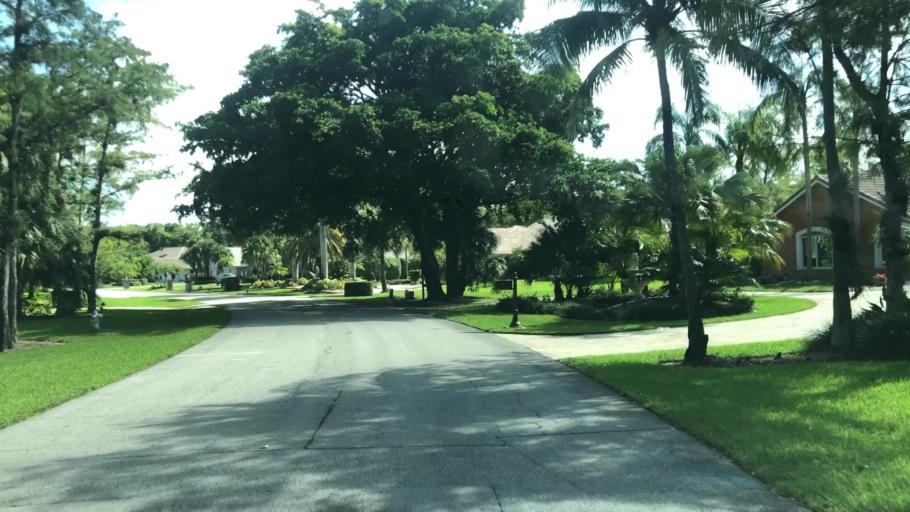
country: US
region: Florida
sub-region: Broward County
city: Parkland
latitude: 26.2923
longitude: -80.2316
